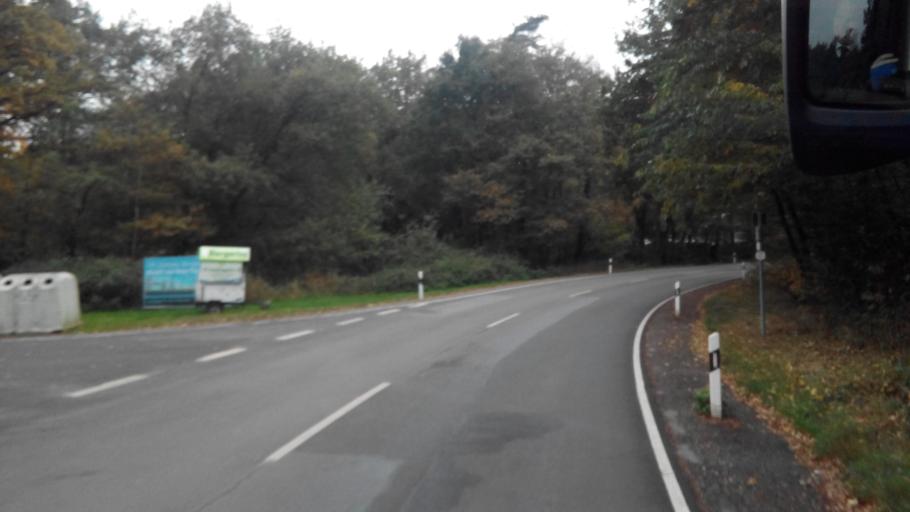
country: DE
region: North Rhine-Westphalia
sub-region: Regierungsbezirk Munster
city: Haltern
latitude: 51.7643
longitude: 7.2308
